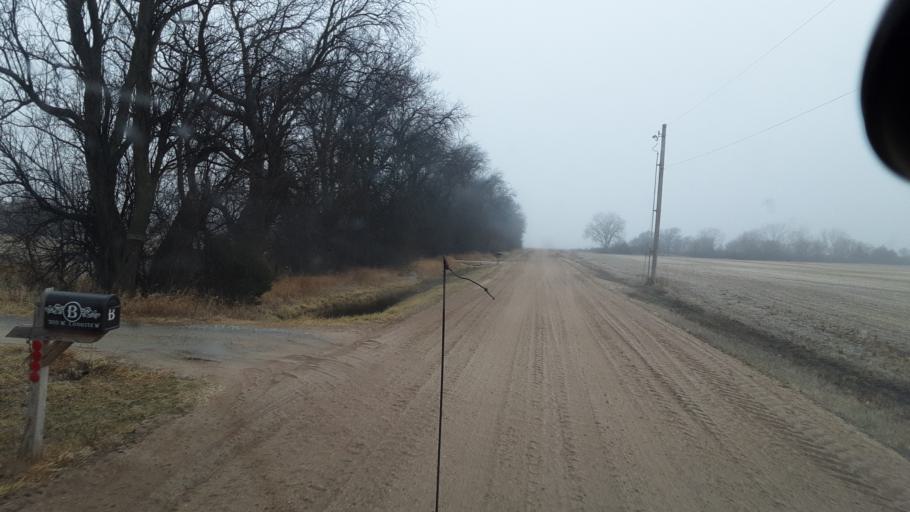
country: US
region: Kansas
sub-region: Reno County
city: South Hutchinson
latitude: 37.9554
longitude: -97.9455
